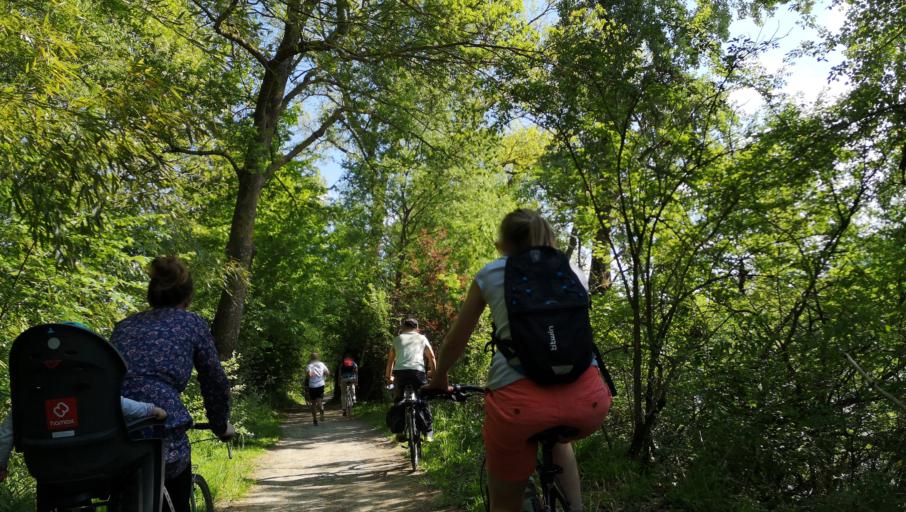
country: FR
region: Midi-Pyrenees
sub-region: Departement de la Haute-Garonne
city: Blagnac
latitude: 43.6396
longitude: 1.4044
